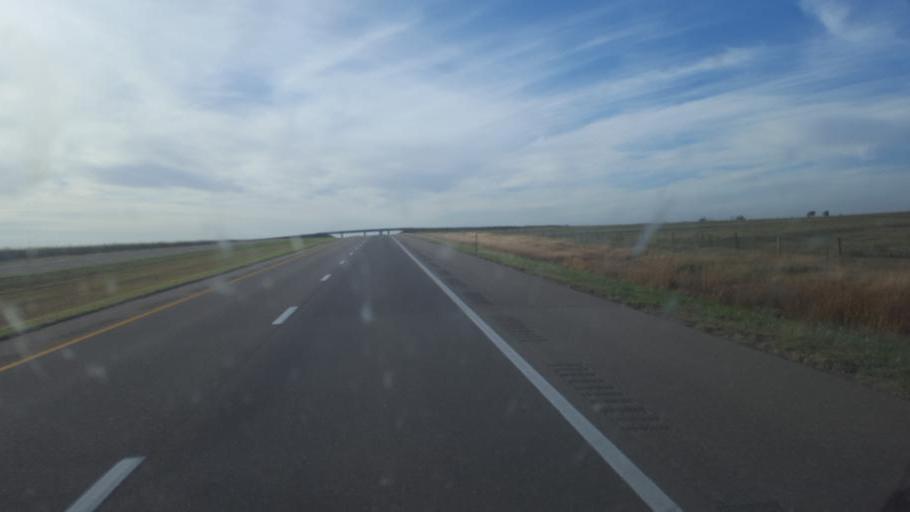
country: US
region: Kansas
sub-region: Gove County
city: Gove
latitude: 39.0727
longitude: -100.2730
